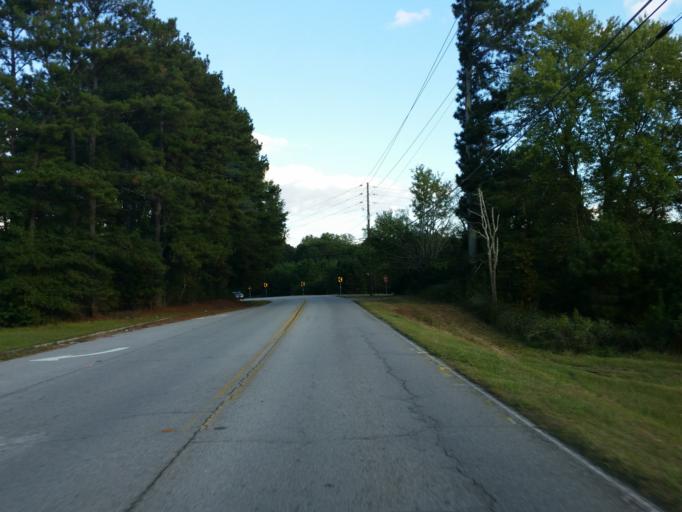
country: US
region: Georgia
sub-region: Paulding County
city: Hiram
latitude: 33.9091
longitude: -84.7536
